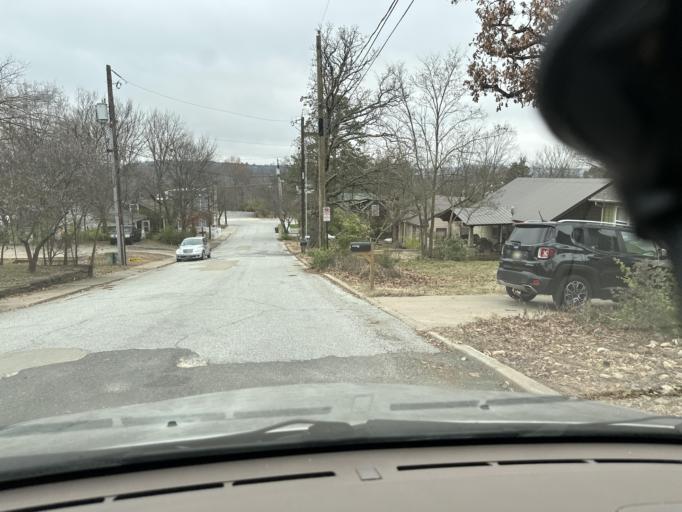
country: US
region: Arkansas
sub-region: Washington County
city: Fayetteville
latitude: 36.0602
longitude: -94.1620
